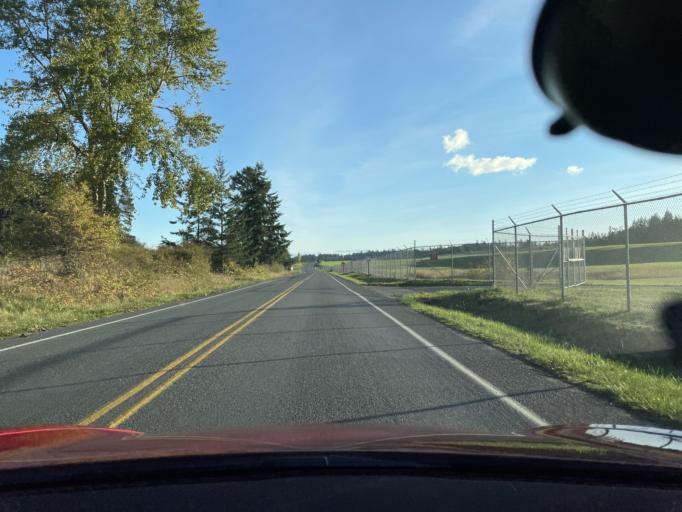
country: US
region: Washington
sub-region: San Juan County
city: Friday Harbor
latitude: 48.5250
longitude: -123.0232
